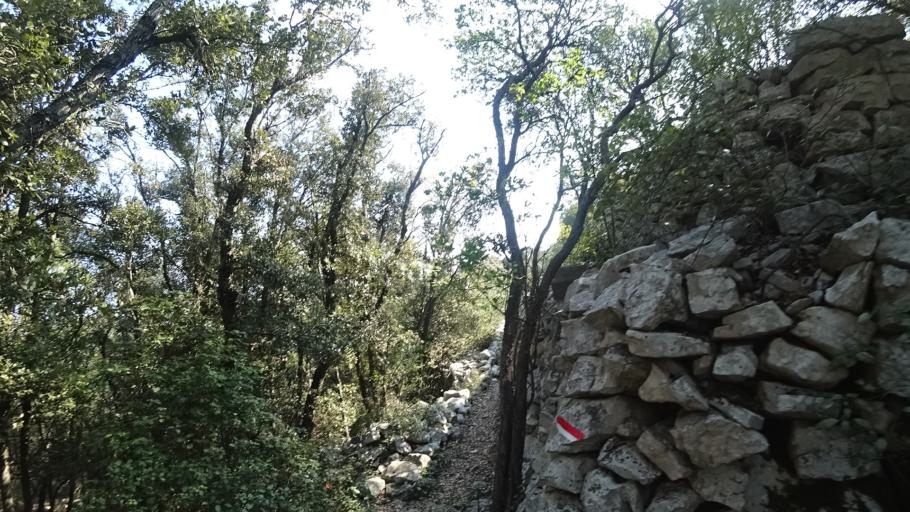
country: HR
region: Primorsko-Goranska
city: Mali Losinj
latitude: 44.4910
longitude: 14.5305
